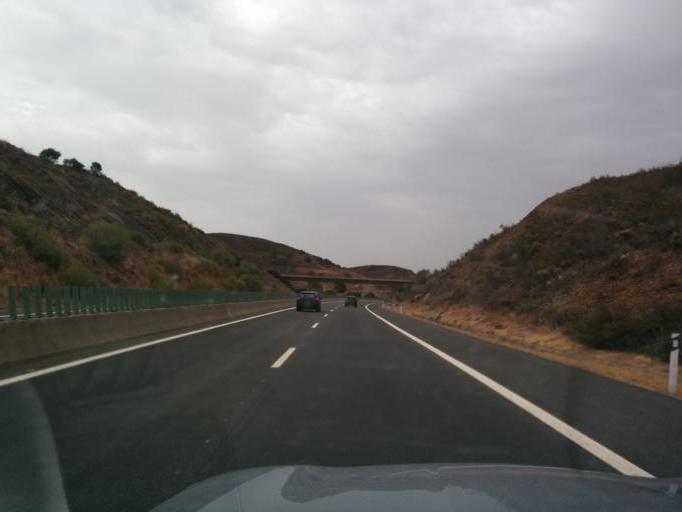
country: PT
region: Faro
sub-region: Tavira
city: Tavira
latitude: 37.1652
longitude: -7.6501
